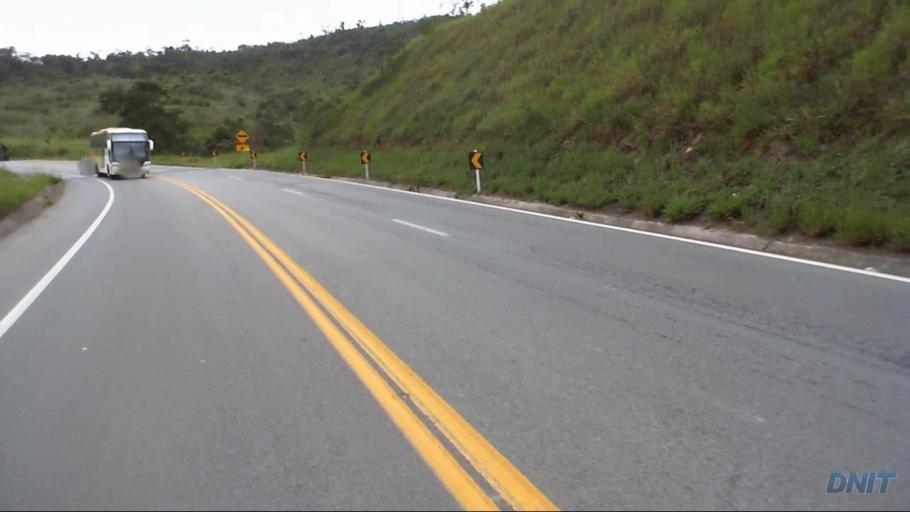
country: BR
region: Minas Gerais
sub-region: Nova Era
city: Nova Era
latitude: -19.6426
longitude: -42.9194
